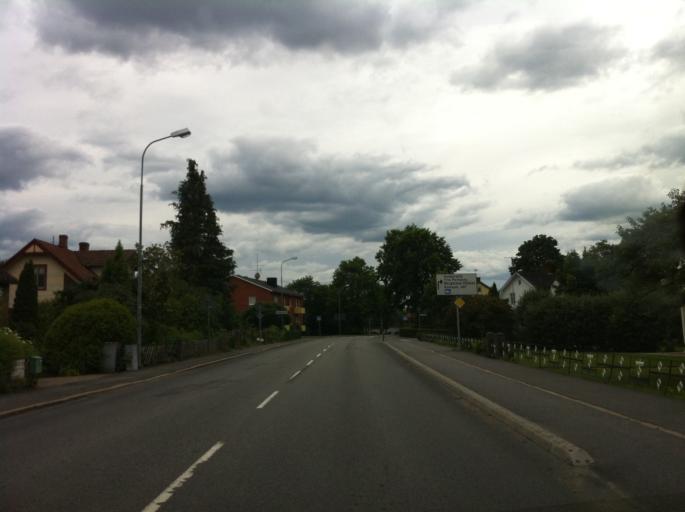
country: SE
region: Skane
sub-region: Osby Kommun
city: Lonsboda
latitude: 56.3999
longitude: 14.3263
